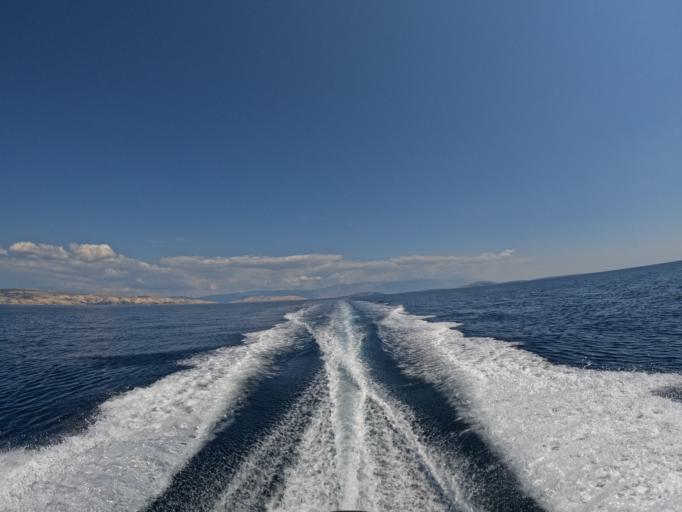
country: HR
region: Primorsko-Goranska
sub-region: Grad Krk
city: Krk
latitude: 44.9213
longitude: 14.5602
